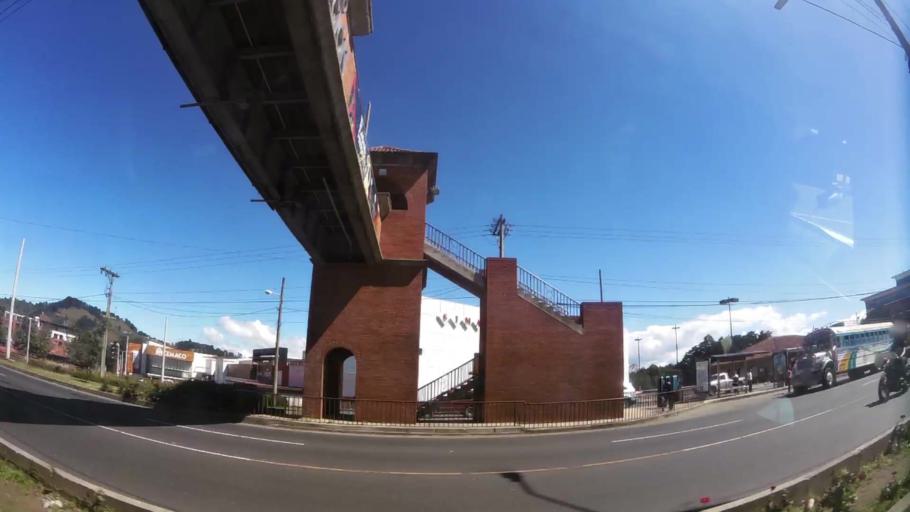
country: GT
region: Guatemala
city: Santa Catarina Pinula
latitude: 14.5512
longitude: -90.4551
